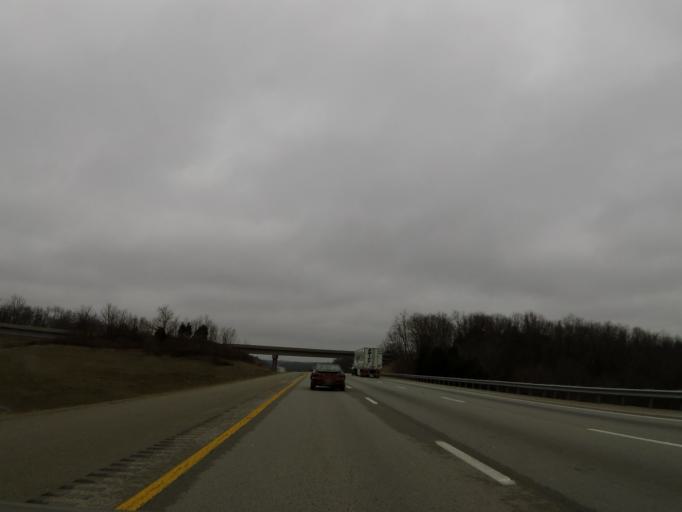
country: US
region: Kentucky
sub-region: Grant County
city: Williamstown
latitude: 38.4342
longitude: -84.5724
